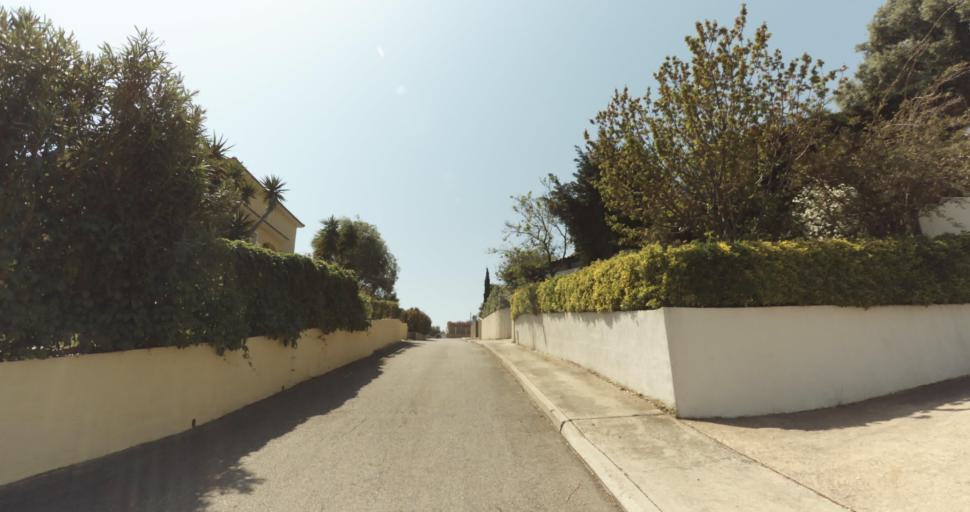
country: FR
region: Corsica
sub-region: Departement de la Haute-Corse
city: Biguglia
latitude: 42.6055
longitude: 9.4279
